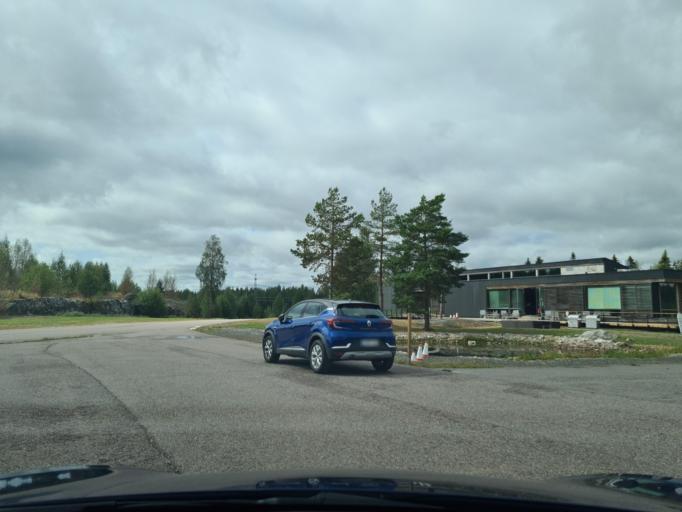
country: FI
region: Uusimaa
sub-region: Helsinki
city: Pornainen
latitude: 60.3455
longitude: 25.4297
